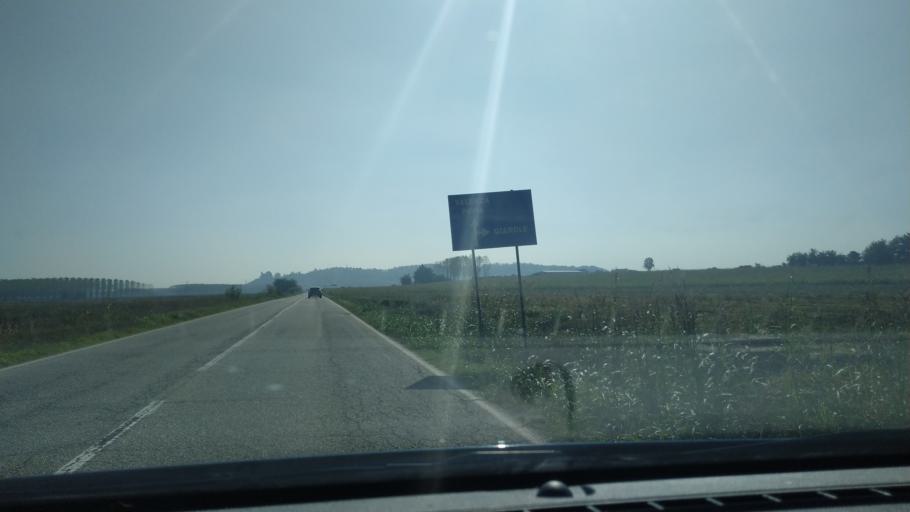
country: IT
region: Piedmont
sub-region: Provincia di Alessandria
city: Giarole
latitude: 45.0763
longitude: 8.5712
